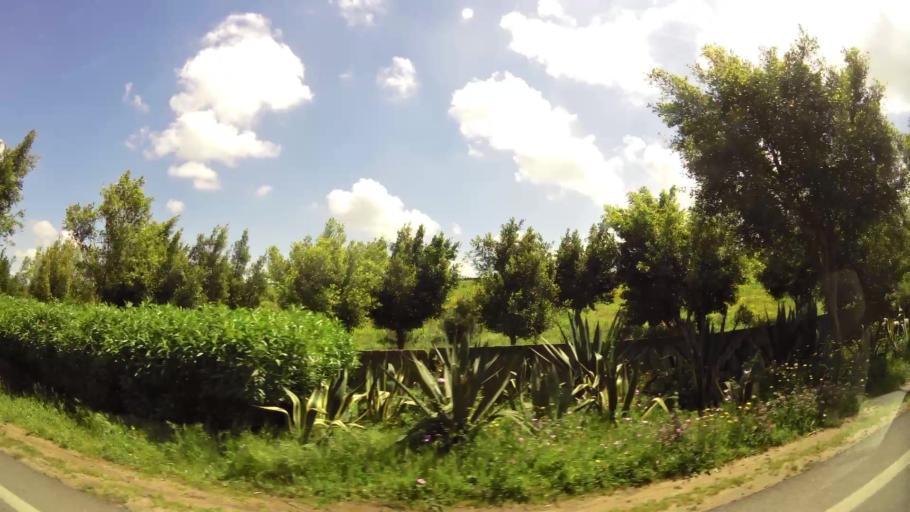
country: MA
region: Grand Casablanca
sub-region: Casablanca
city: Casablanca
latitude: 33.5281
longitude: -7.5681
